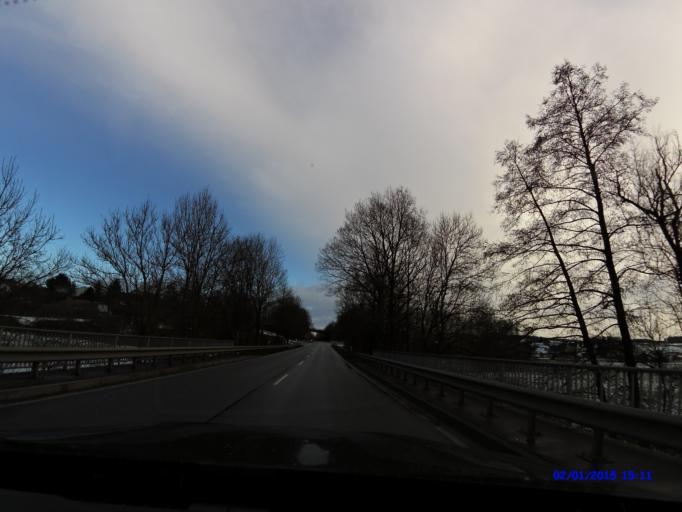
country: DE
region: Bavaria
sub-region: Lower Bavaria
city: Mainburg
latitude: 48.6288
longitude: 11.7811
